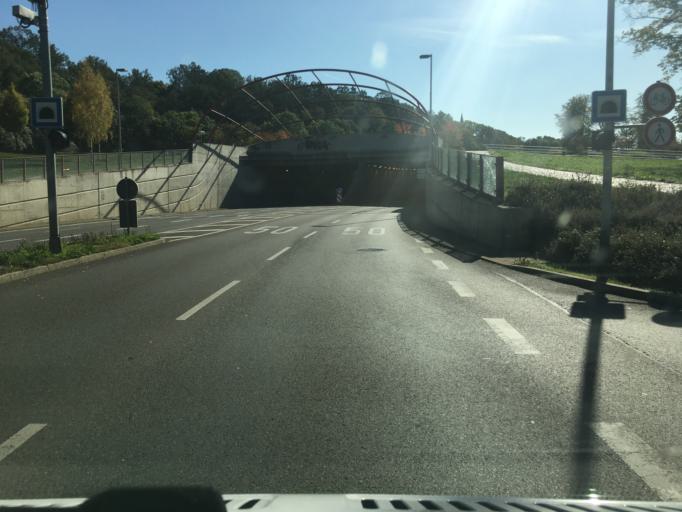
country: DE
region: Saxony
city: Zwickau
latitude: 50.7217
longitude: 12.5016
